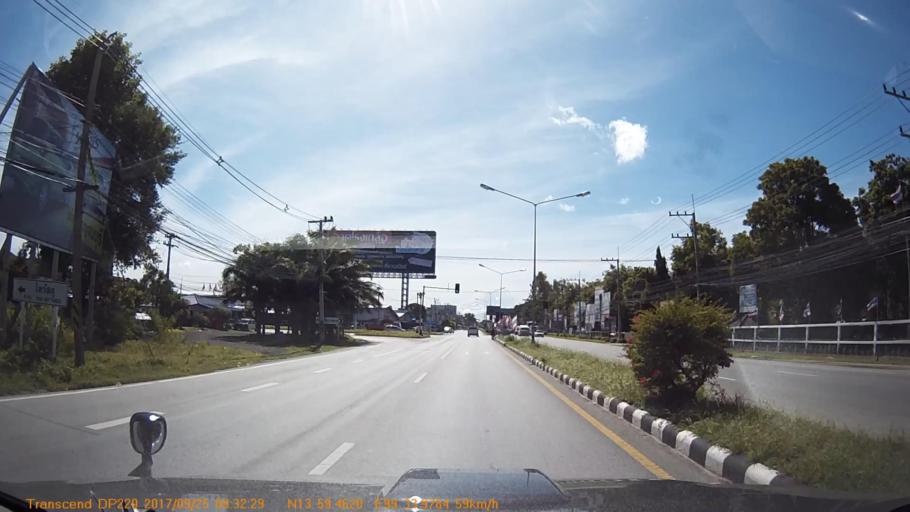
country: TH
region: Kanchanaburi
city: Kanchanaburi
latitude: 13.9909
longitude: 99.5664
